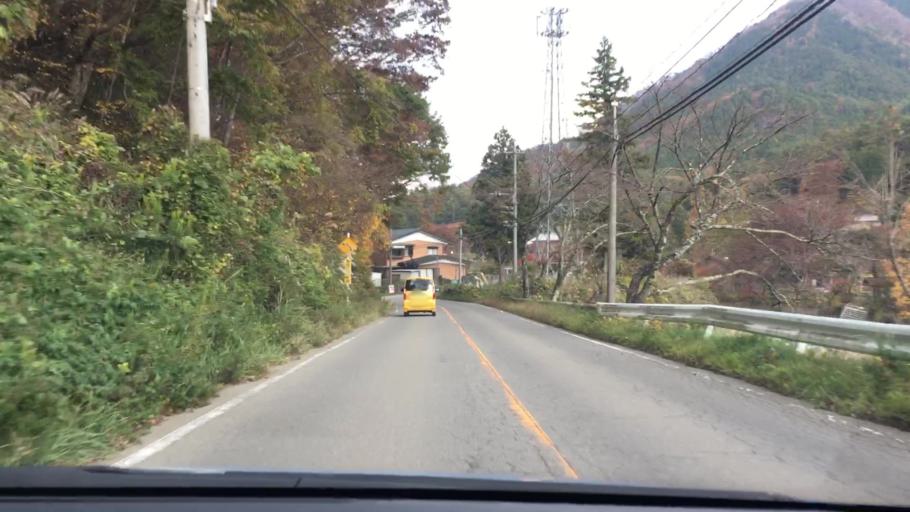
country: JP
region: Yamanashi
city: Otsuki
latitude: 35.4993
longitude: 138.9860
